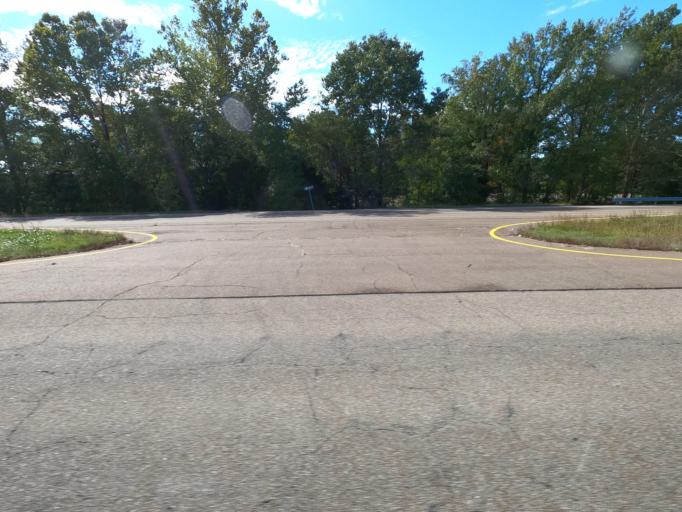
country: US
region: Tennessee
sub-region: Lauderdale County
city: Halls
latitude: 35.8956
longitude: -89.2418
